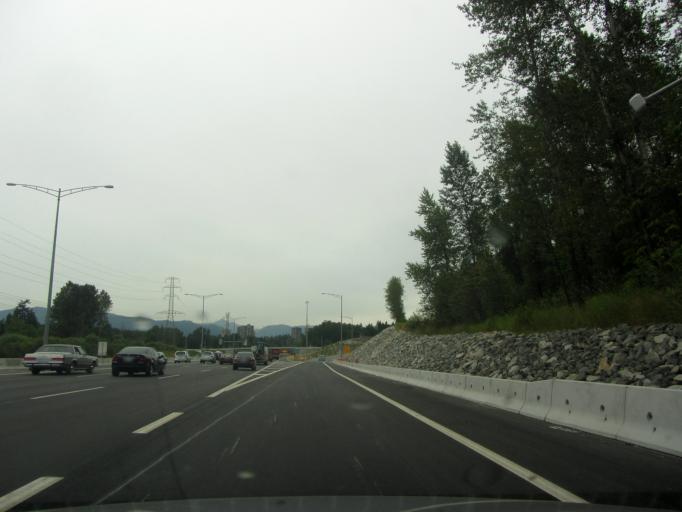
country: CA
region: British Columbia
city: Burnaby
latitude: 49.2429
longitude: -122.9666
